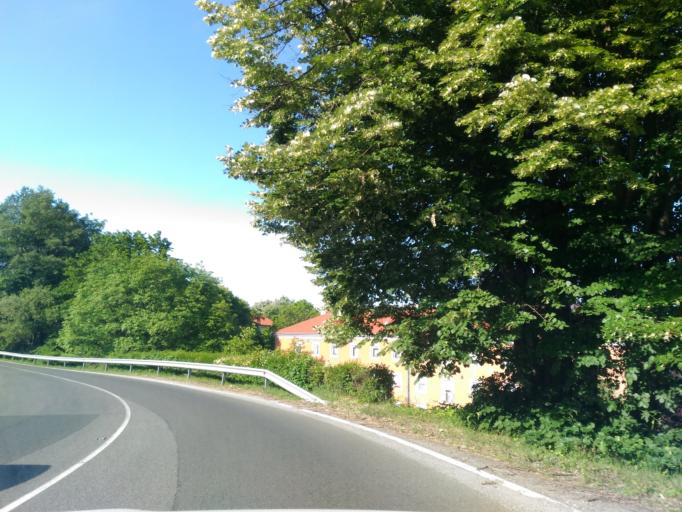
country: HU
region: Baranya
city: Komlo
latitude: 46.1829
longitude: 18.2620
